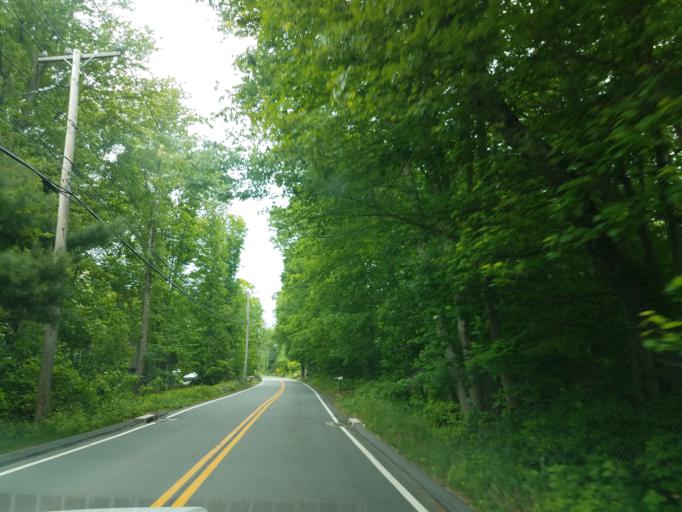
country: US
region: Rhode Island
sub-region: Washington County
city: Ashaway
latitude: 41.4423
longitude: -71.8483
